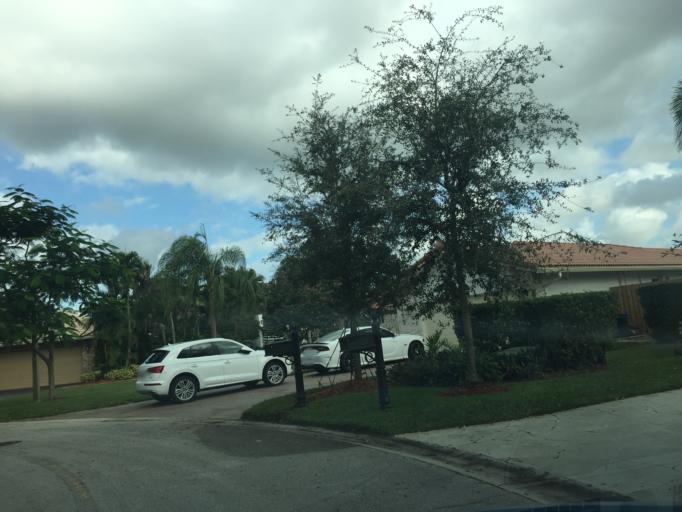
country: US
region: Florida
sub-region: Broward County
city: Tamarac
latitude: 26.2319
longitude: -80.2503
